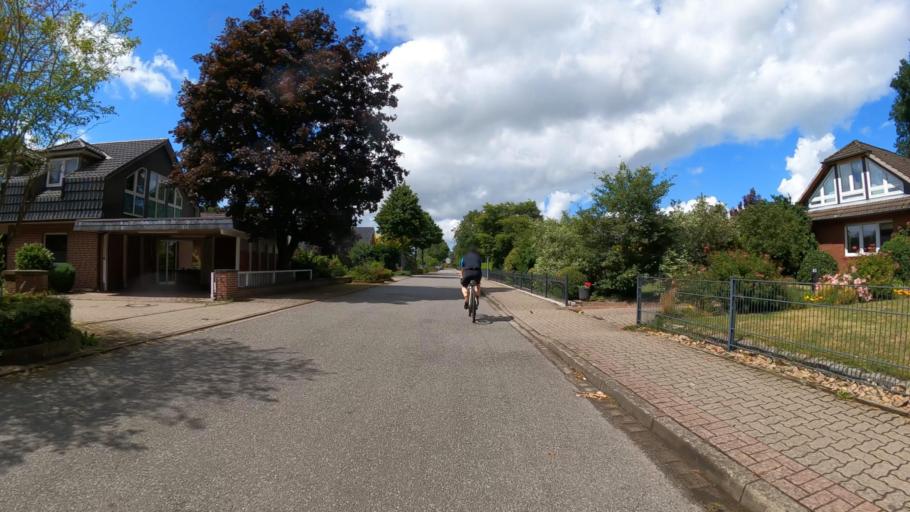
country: DE
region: Lower Saxony
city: Neu Wulmstorf
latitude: 53.4208
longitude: 9.7959
